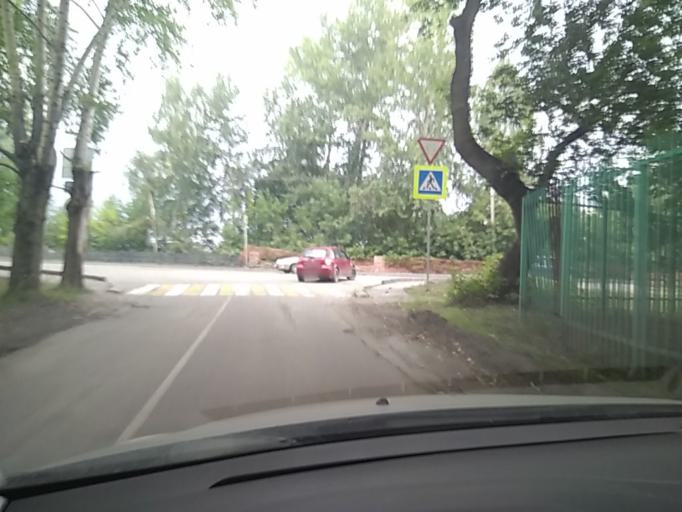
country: RU
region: Chelyabinsk
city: Kyshtym
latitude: 55.7034
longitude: 60.5298
